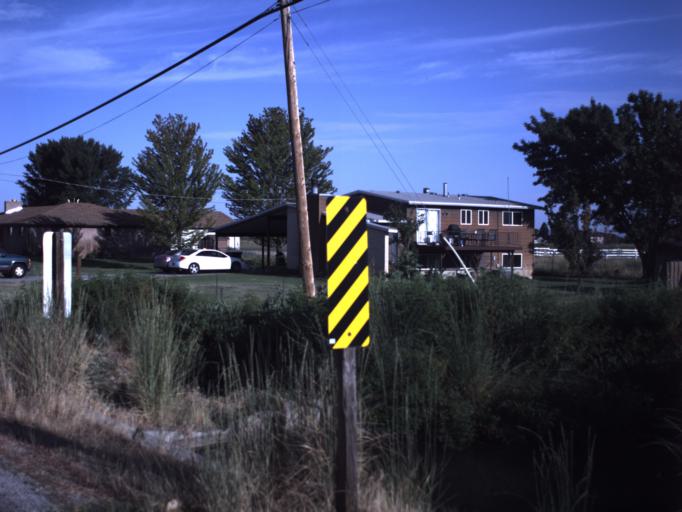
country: US
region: Utah
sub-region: Weber County
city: Plain City
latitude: 41.3053
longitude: -112.0707
